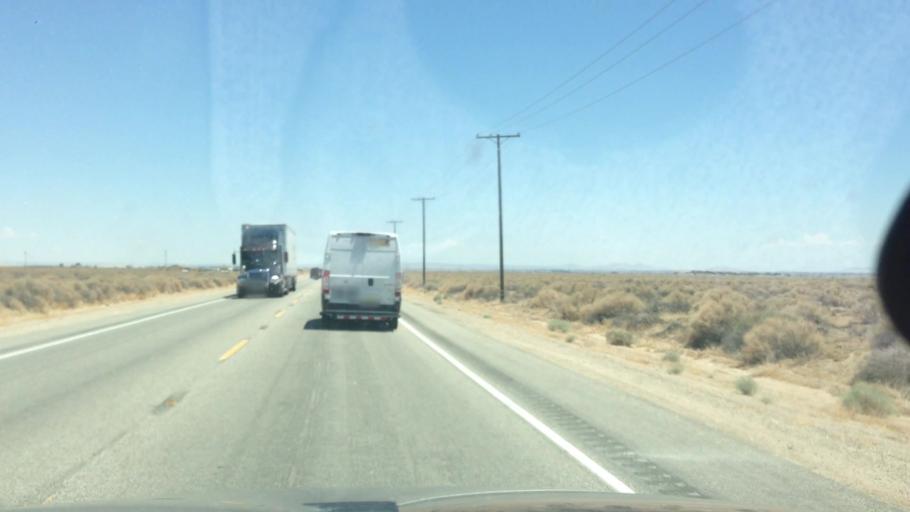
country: US
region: California
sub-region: Kern County
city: Rosamond
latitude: 34.7765
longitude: -118.2176
